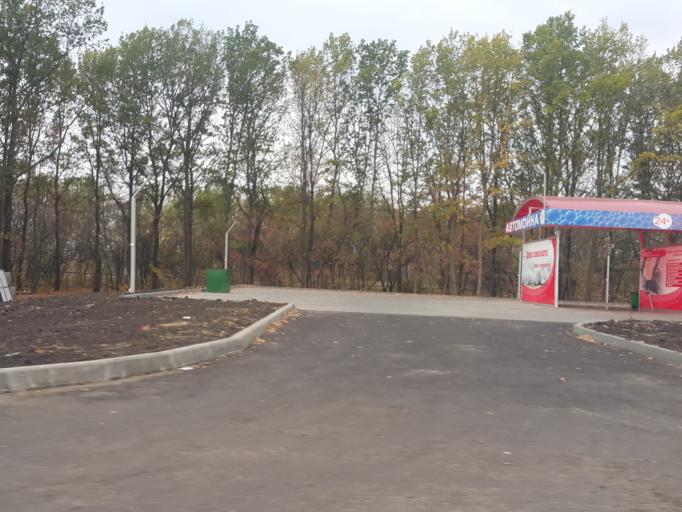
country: RU
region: Tambov
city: Bokino
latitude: 52.6392
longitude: 41.4396
